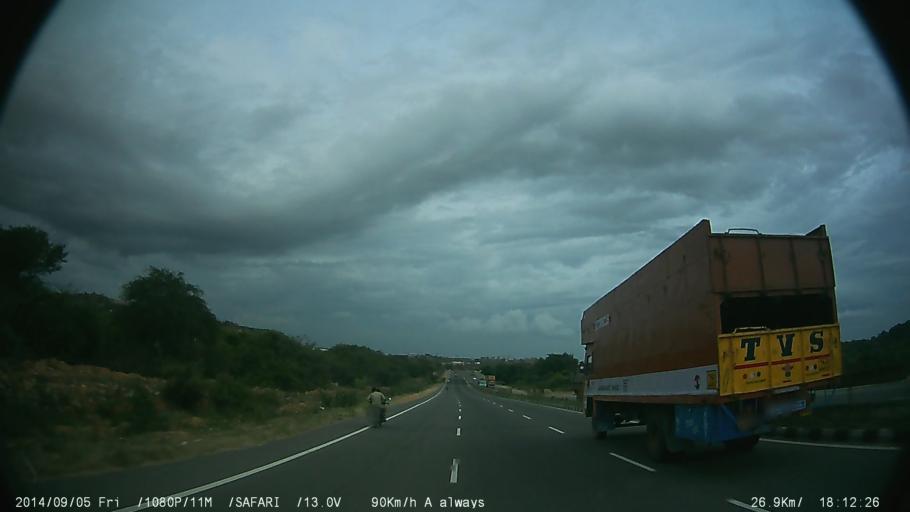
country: IN
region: Tamil Nadu
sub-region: Krishnagiri
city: Hosur
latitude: 12.6925
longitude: 77.9181
